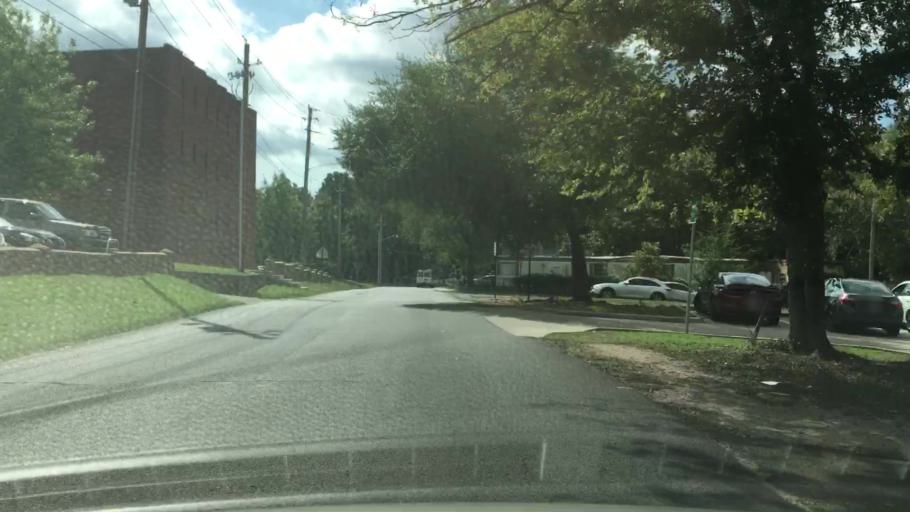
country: US
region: Oklahoma
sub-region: Cherokee County
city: Tahlequah
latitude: 35.9204
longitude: -94.9711
